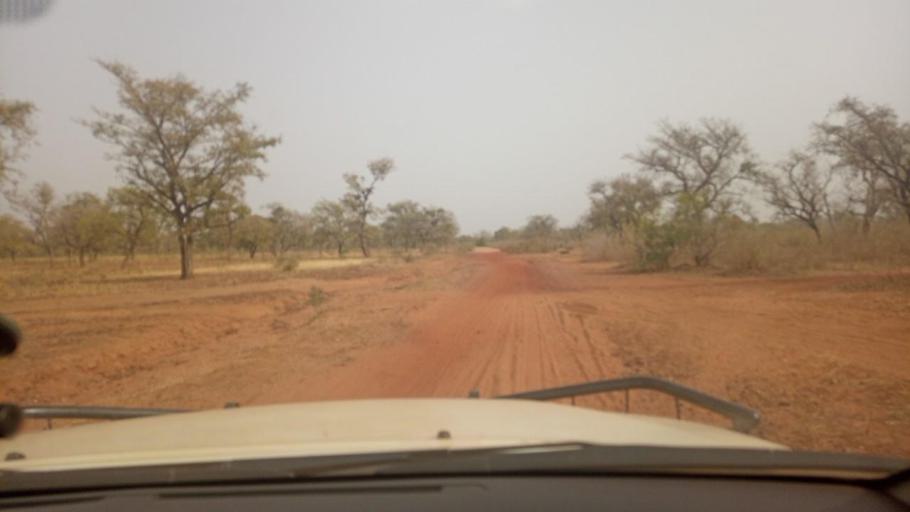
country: BF
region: Boucle du Mouhoun
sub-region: Province des Banwa
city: Salanso
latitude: 12.0981
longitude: -4.3328
